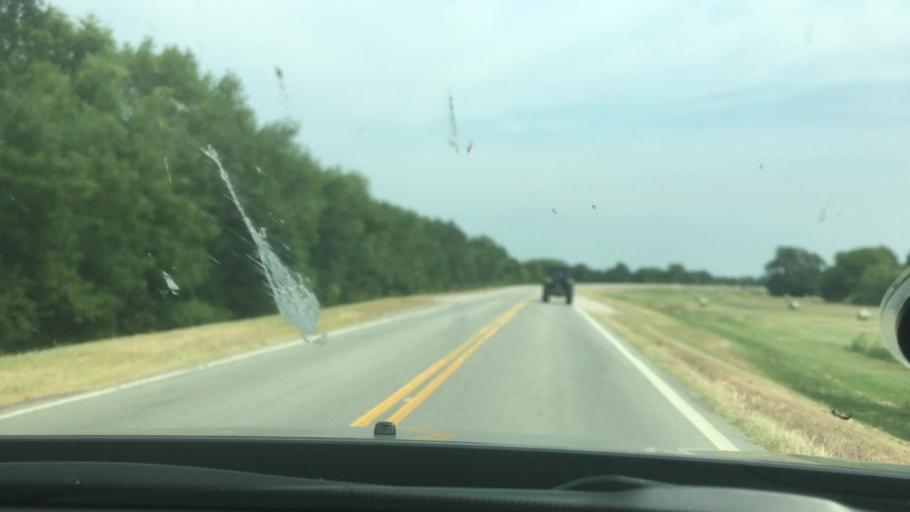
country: US
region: Oklahoma
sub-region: Coal County
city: Coalgate
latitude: 34.5376
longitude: -96.4078
